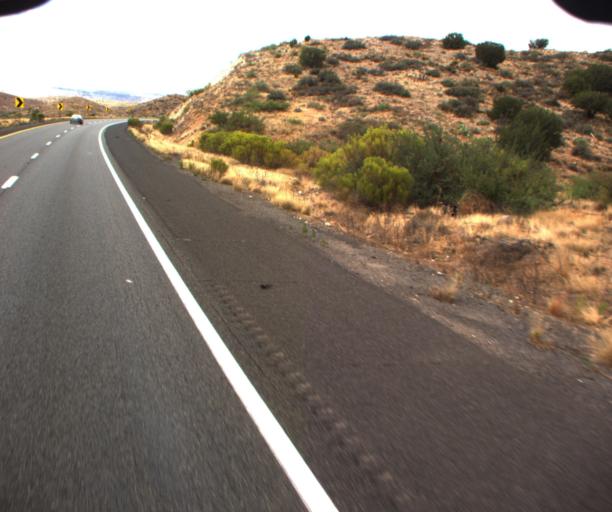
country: US
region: Arizona
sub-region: Yavapai County
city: Cordes Lakes
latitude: 34.2736
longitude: -112.1152
